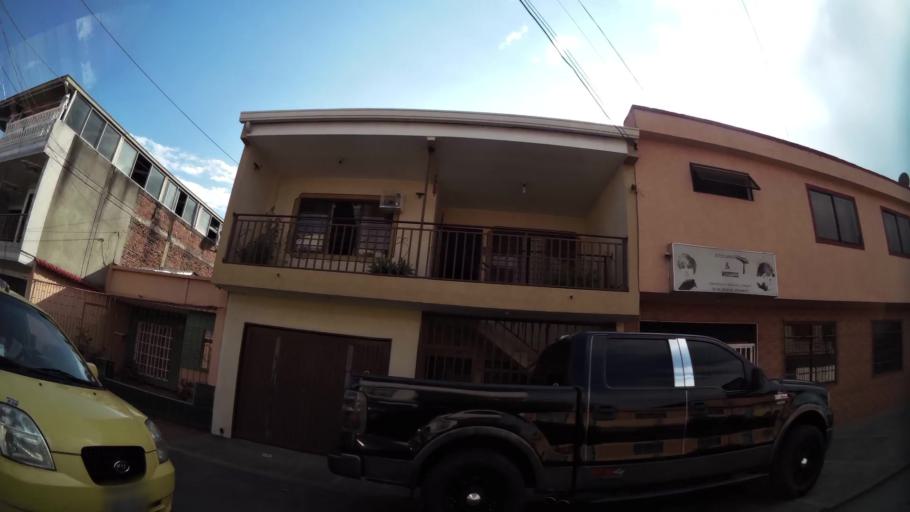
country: CO
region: Valle del Cauca
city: Cali
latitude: 3.4305
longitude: -76.5250
